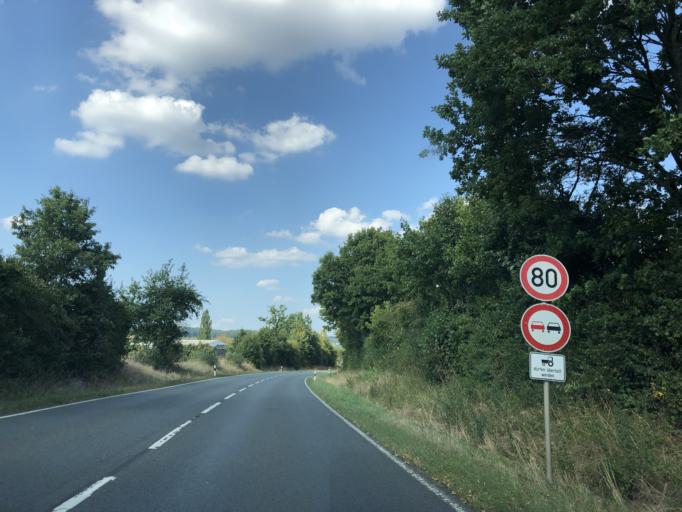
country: DE
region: Hesse
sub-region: Regierungsbezirk Giessen
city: Kirchhain
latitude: 50.8322
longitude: 8.9208
